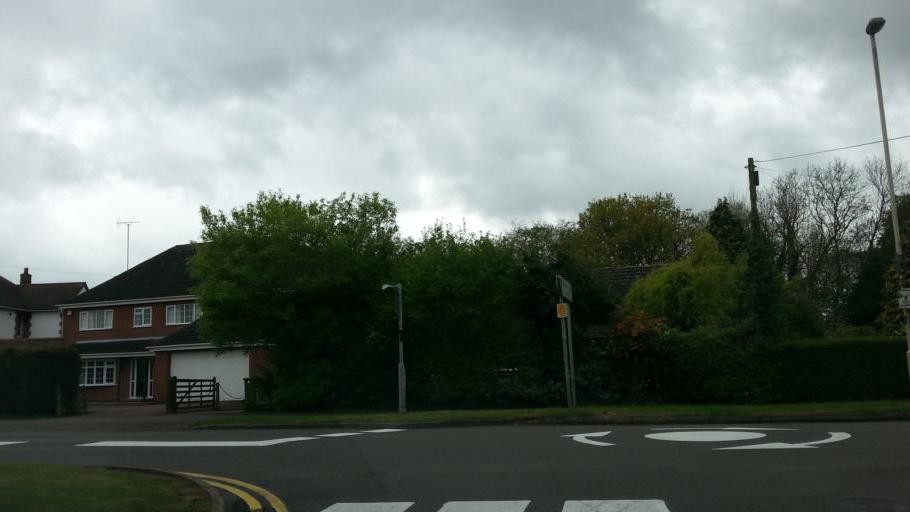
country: GB
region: England
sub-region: Leicestershire
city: Lutterworth
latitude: 52.4589
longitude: -1.2044
